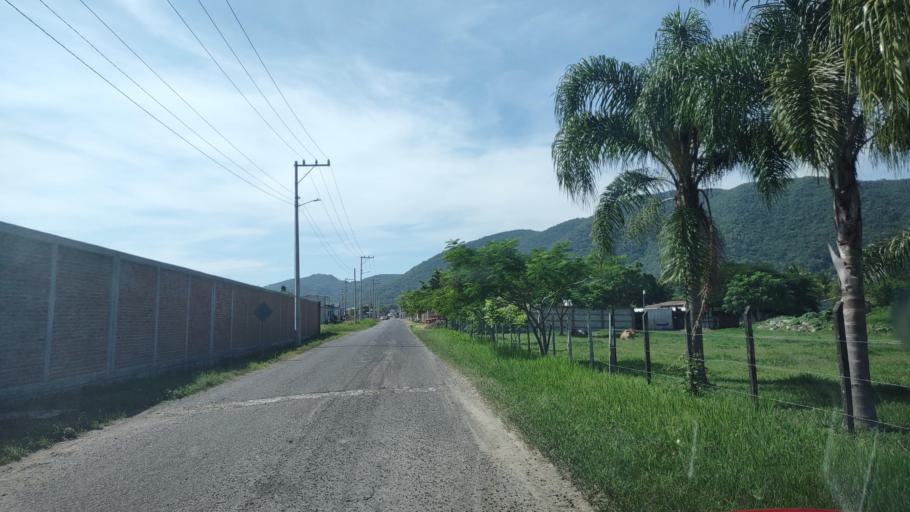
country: MX
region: Veracruz
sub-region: Emiliano Zapata
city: Dos Rios
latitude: 19.4312
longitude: -96.8018
